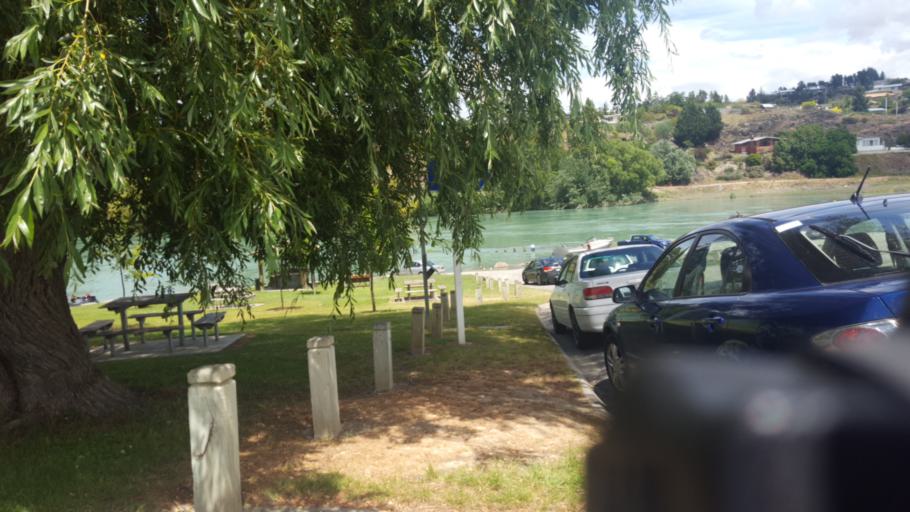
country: NZ
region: Otago
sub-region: Queenstown-Lakes District
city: Wanaka
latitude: -45.2570
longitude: 169.3892
